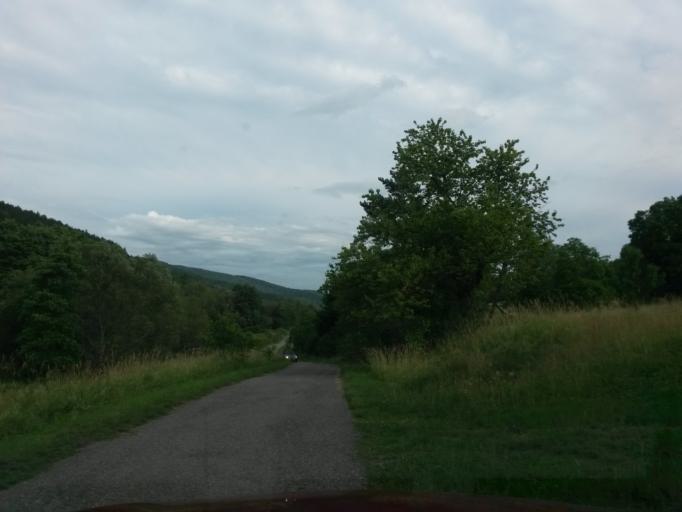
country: SK
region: Banskobystricky
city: Detva
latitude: 48.4358
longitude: 19.3458
